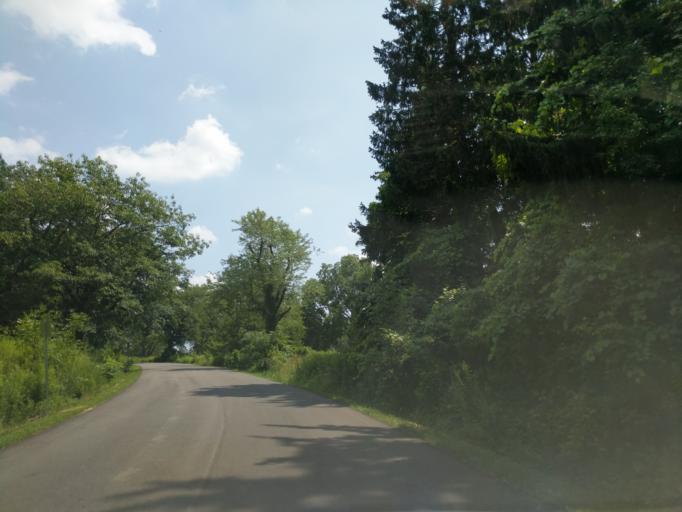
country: CA
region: Ontario
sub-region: York
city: Richmond Hill
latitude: 43.8624
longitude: -79.4241
